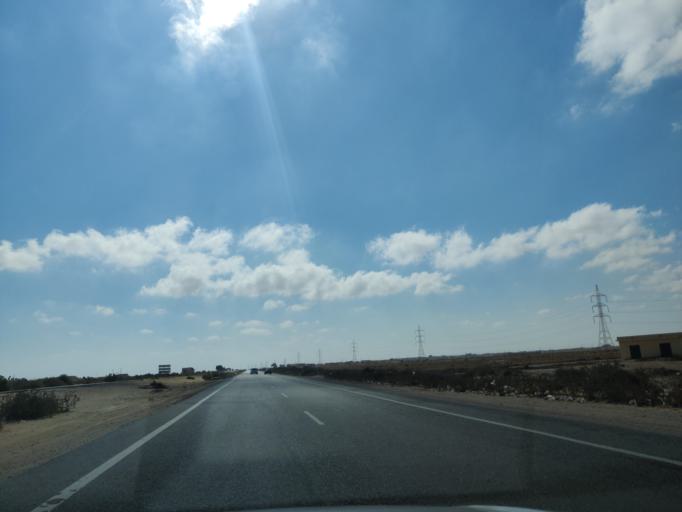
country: EG
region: Muhafazat Matruh
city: Al `Alamayn
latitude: 31.0540
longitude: 28.2743
